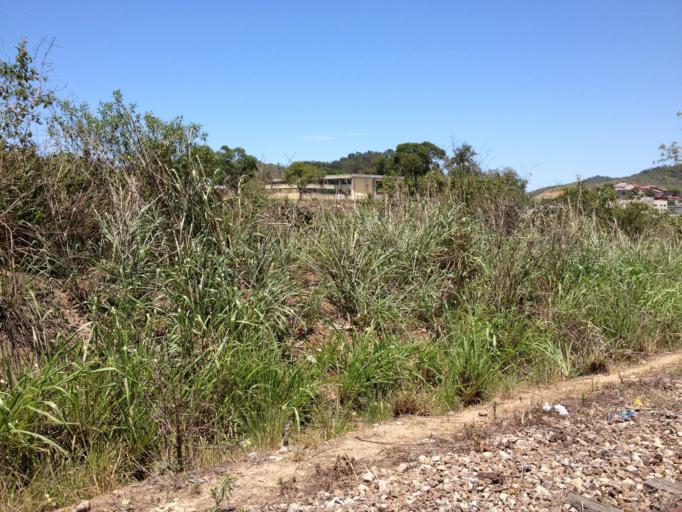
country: BR
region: Rio de Janeiro
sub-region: Rio Bonito
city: Rio Bonito
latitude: -22.7089
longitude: -42.6437
